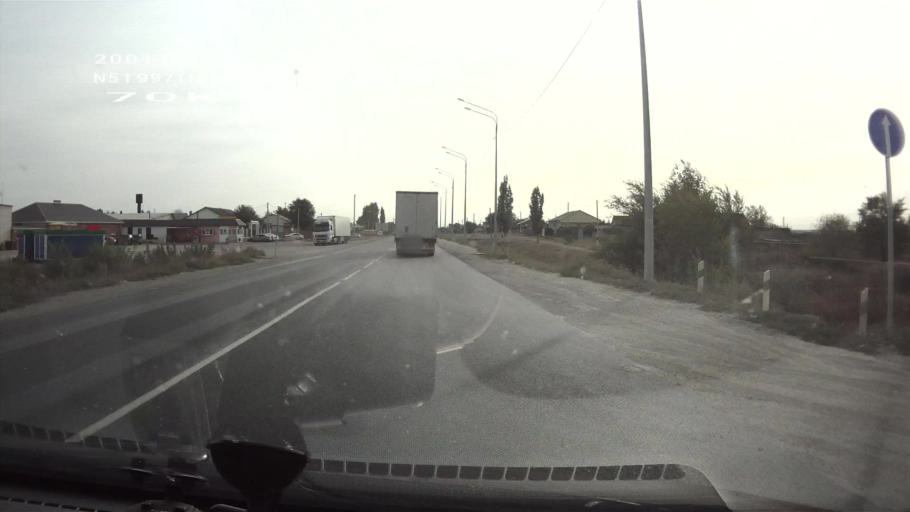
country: RU
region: Saratov
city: Sinodskoye
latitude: 51.9966
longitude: 46.6741
